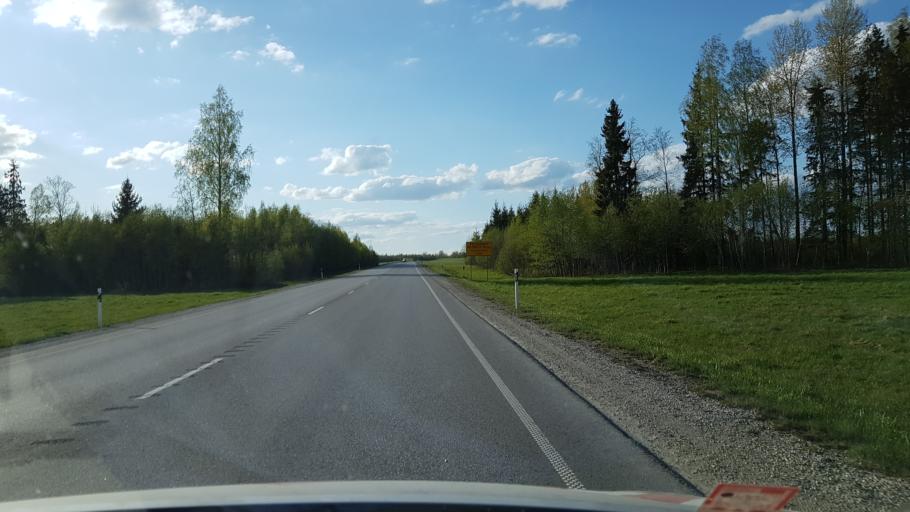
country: EE
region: Vorumaa
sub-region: Voru linn
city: Voru
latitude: 57.9182
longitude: 26.8121
